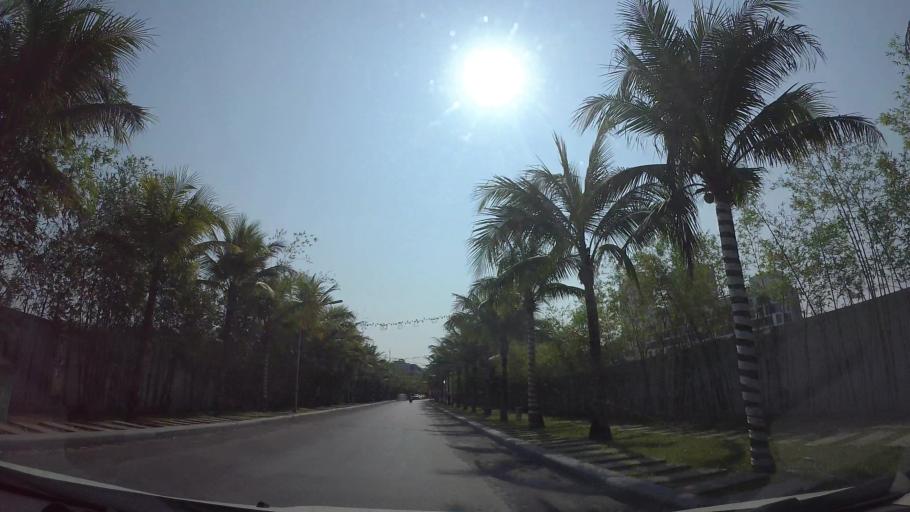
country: VN
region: Da Nang
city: Ngu Hanh Son
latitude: 15.9647
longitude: 108.2826
